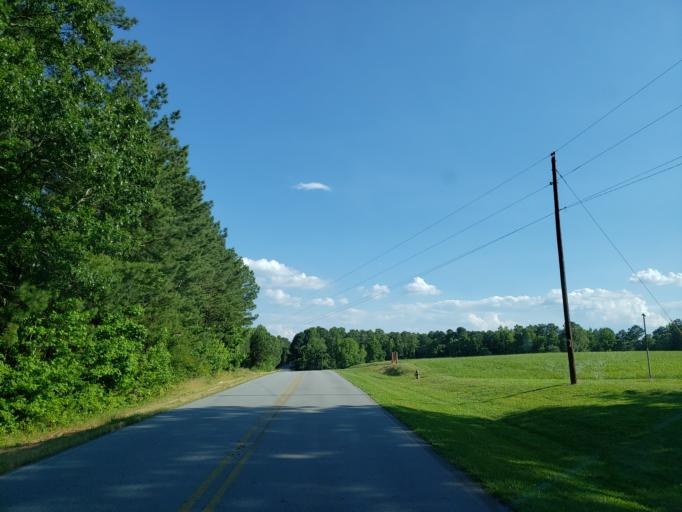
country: US
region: Georgia
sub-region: Haralson County
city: Bremen
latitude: 33.6682
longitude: -85.0856
